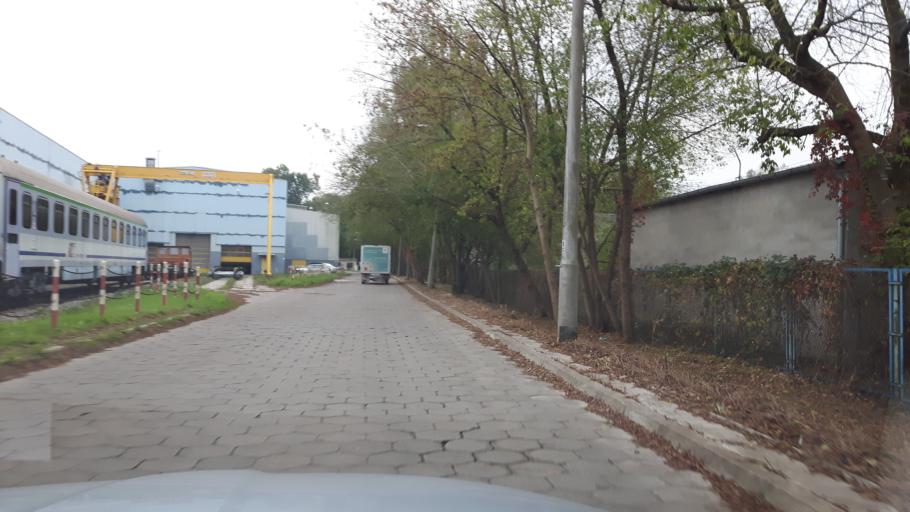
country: PL
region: Masovian Voivodeship
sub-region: Warszawa
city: Praga Poludnie
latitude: 52.2509
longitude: 21.1138
